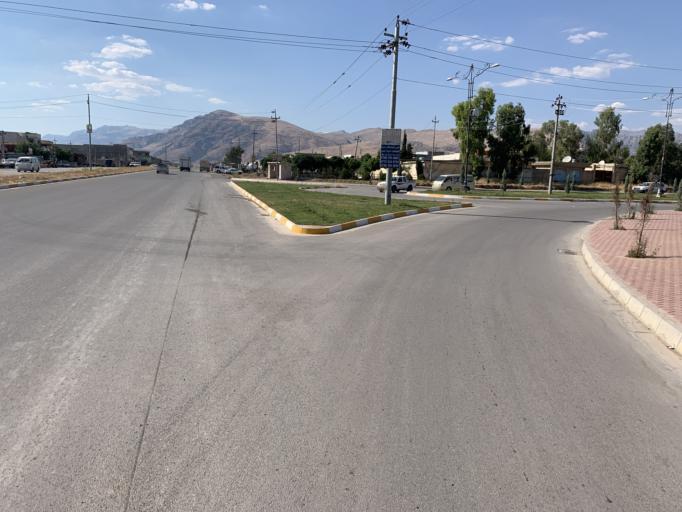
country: IQ
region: As Sulaymaniyah
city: Raniye
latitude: 36.2315
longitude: 44.7864
